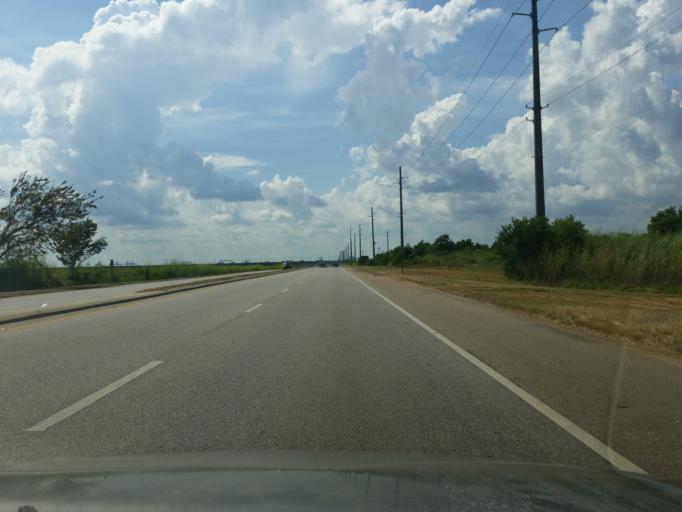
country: US
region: Alabama
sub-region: Baldwin County
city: Spanish Fort
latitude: 30.6751
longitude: -87.9677
